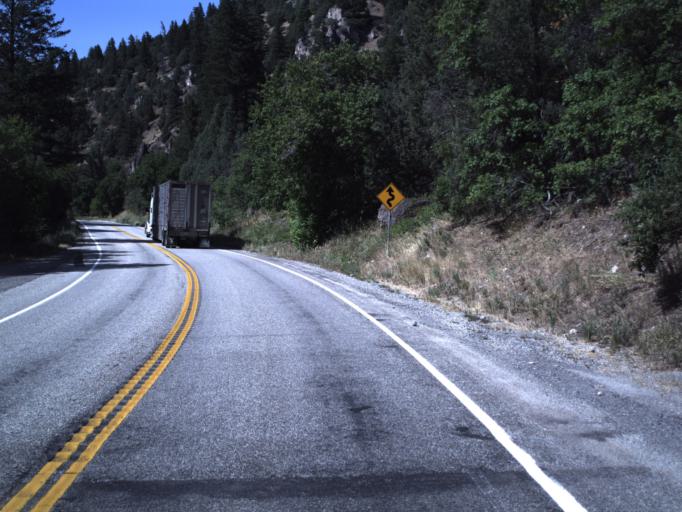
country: US
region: Utah
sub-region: Cache County
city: North Logan
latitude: 41.7843
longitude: -111.6410
